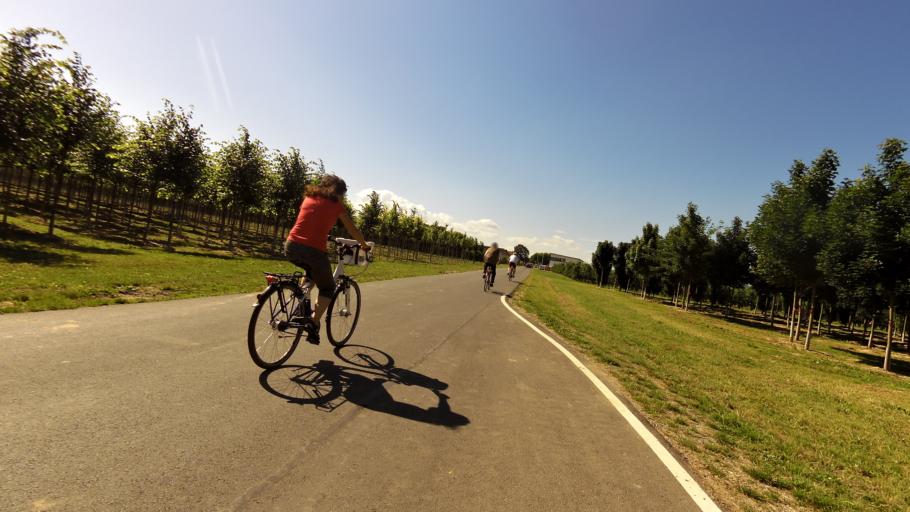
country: DE
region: North Rhine-Westphalia
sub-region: Regierungsbezirk Koln
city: Rheinbach
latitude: 50.6277
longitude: 6.9878
